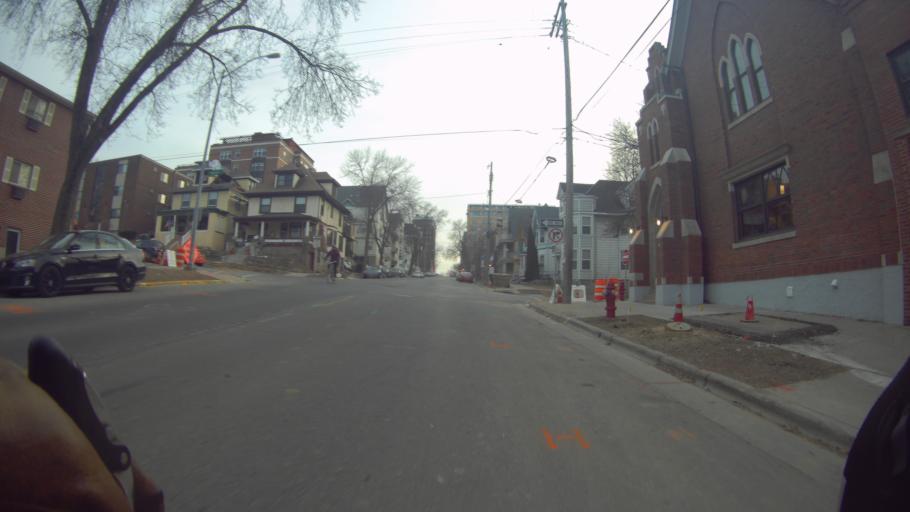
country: US
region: Wisconsin
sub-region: Dane County
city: Madison
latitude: 43.0783
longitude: -89.3812
